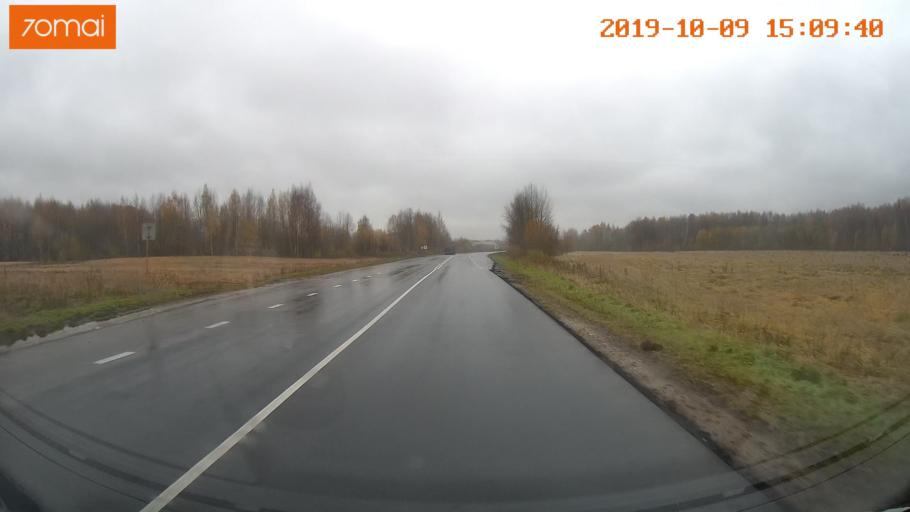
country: RU
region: Kostroma
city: Susanino
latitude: 58.1883
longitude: 41.6492
